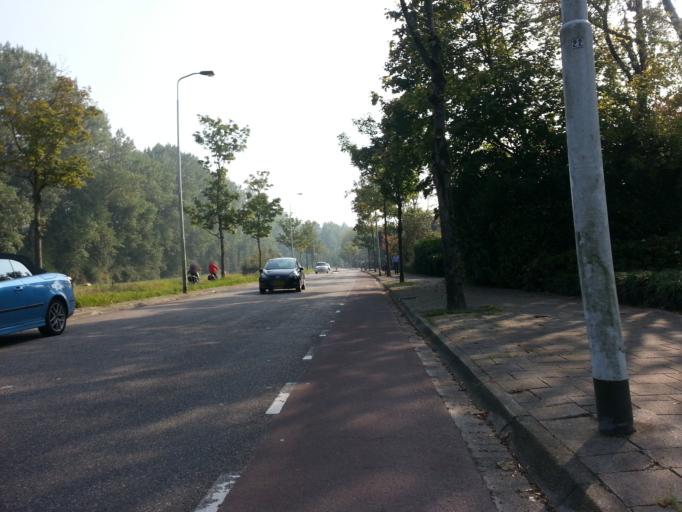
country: NL
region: North Brabant
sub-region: Gemeente Eindhoven
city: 't Hofke
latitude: 51.4712
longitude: 5.5037
